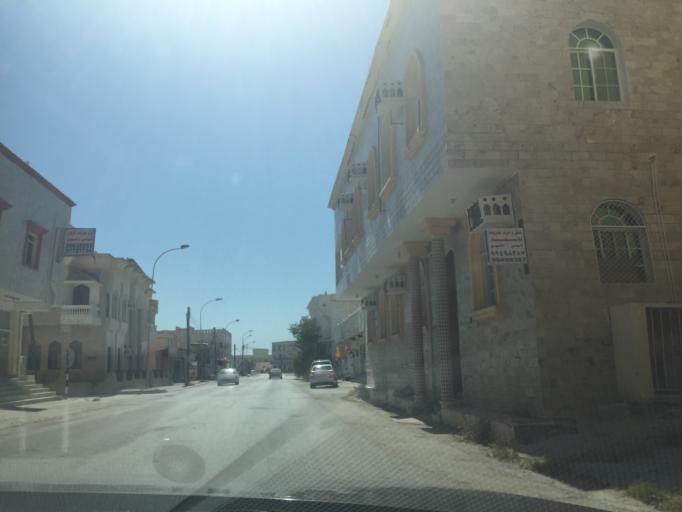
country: OM
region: Zufar
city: Salalah
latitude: 17.0236
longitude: 54.1564
